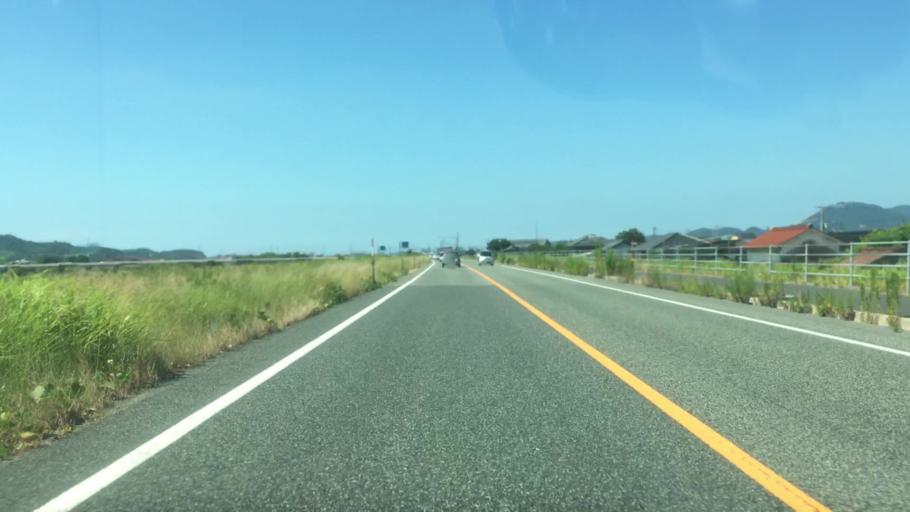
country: JP
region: Tottori
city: Tottori
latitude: 35.4584
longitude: 134.2152
